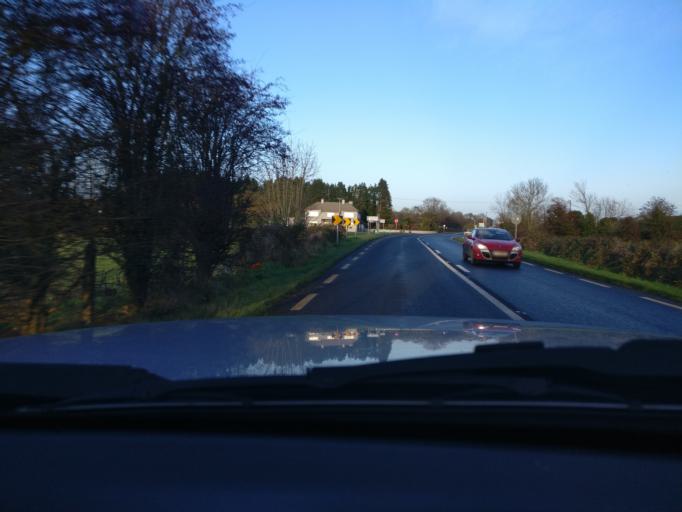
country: IE
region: Leinster
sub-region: Lu
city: Ardee
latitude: 53.8174
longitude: -6.6491
